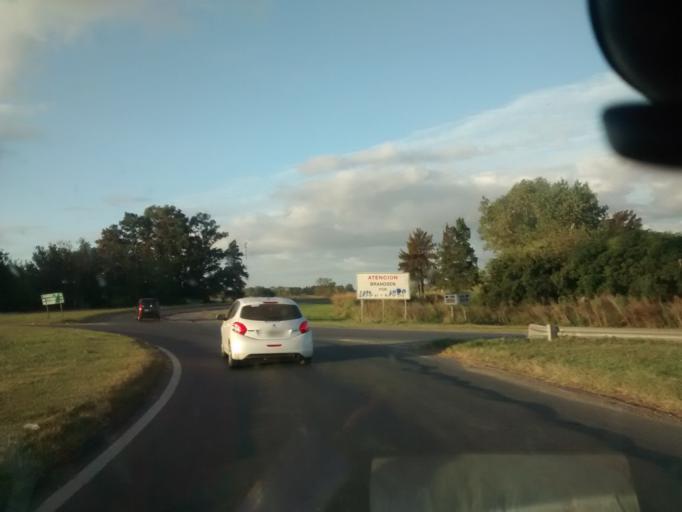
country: AR
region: Buenos Aires
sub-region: Partido de General Belgrano
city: General Belgrano
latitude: -35.7692
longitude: -58.5140
